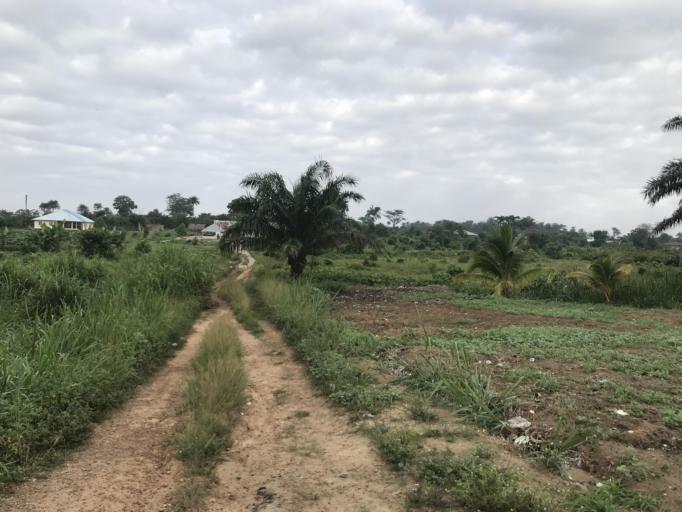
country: SL
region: Eastern Province
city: Pendembu
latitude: 8.0855
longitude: -10.6915
